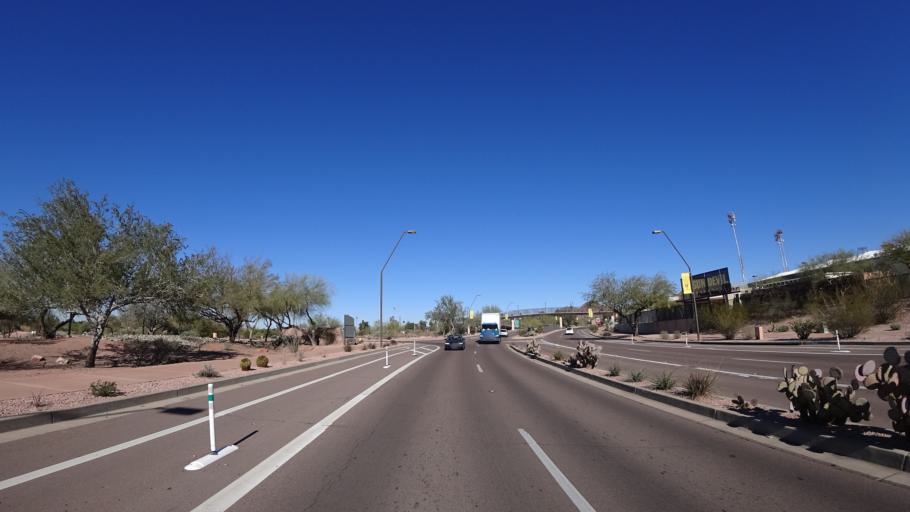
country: US
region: Arizona
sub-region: Maricopa County
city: Tempe Junction
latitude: 33.4484
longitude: -111.9561
